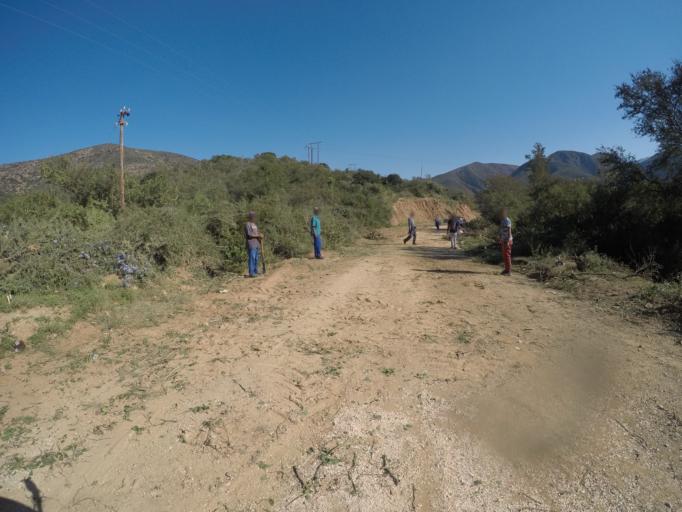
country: ZA
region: Eastern Cape
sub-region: Cacadu District Municipality
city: Kruisfontein
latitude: -33.6651
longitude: 24.5624
